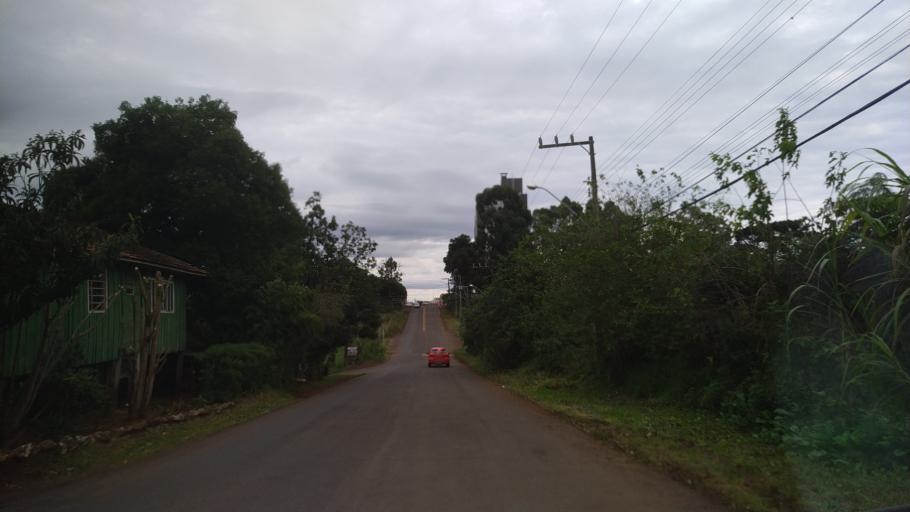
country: BR
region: Santa Catarina
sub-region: Chapeco
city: Chapeco
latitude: -27.0723
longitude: -52.6073
